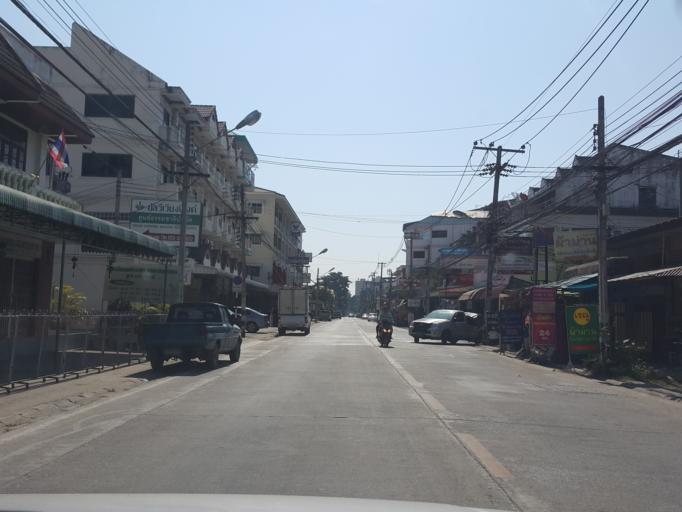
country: TH
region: Chiang Mai
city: Chiang Mai
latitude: 18.7992
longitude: 99.0146
